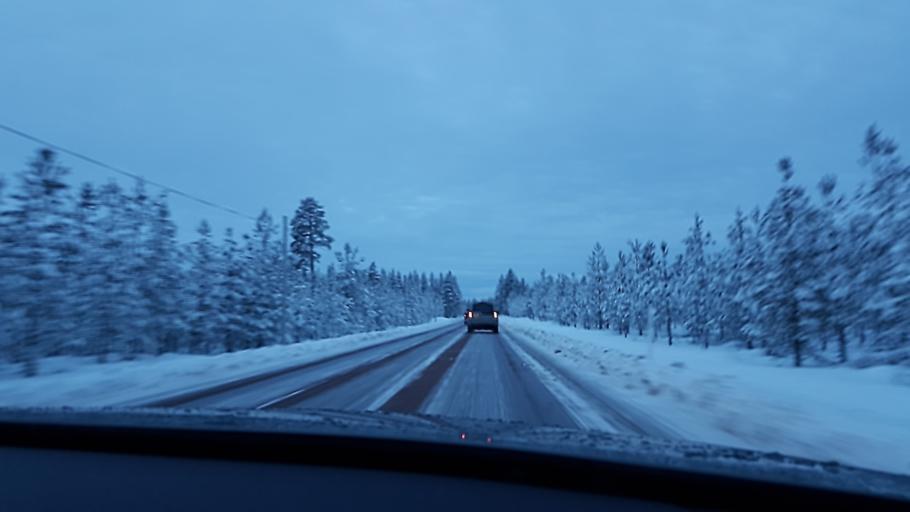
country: SE
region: Jaemtland
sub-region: Harjedalens Kommun
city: Sveg
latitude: 62.0563
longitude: 14.5954
